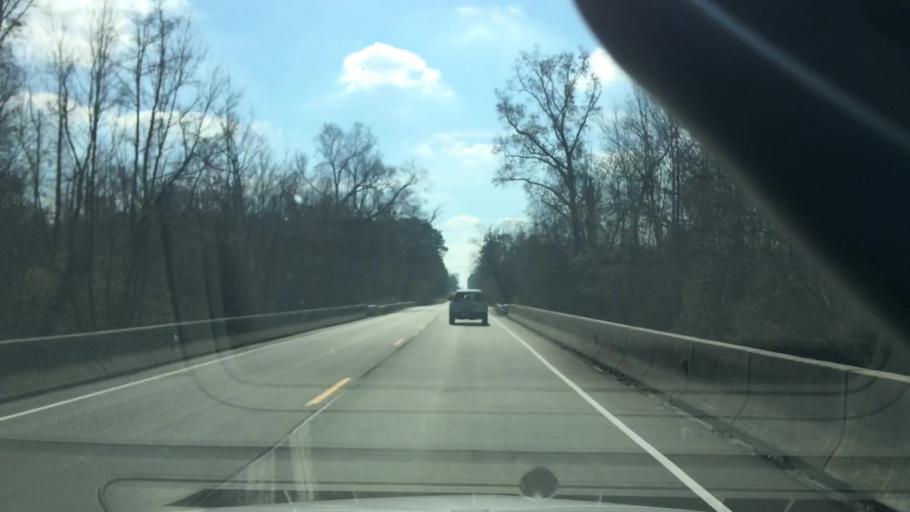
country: US
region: North Carolina
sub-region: Duplin County
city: Beulaville
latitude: 34.9424
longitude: -77.7691
